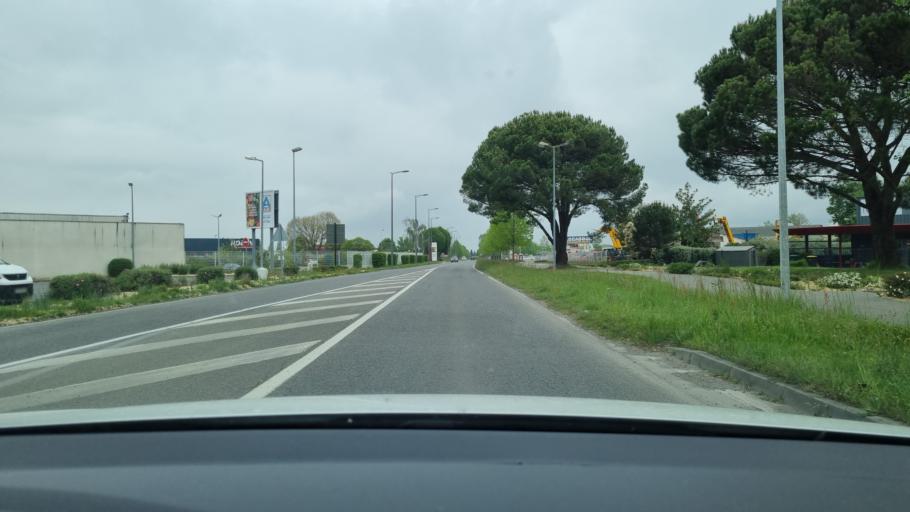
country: FR
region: Aquitaine
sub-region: Departement des Pyrenees-Atlantiques
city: Montardon
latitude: 43.3591
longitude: -0.3821
